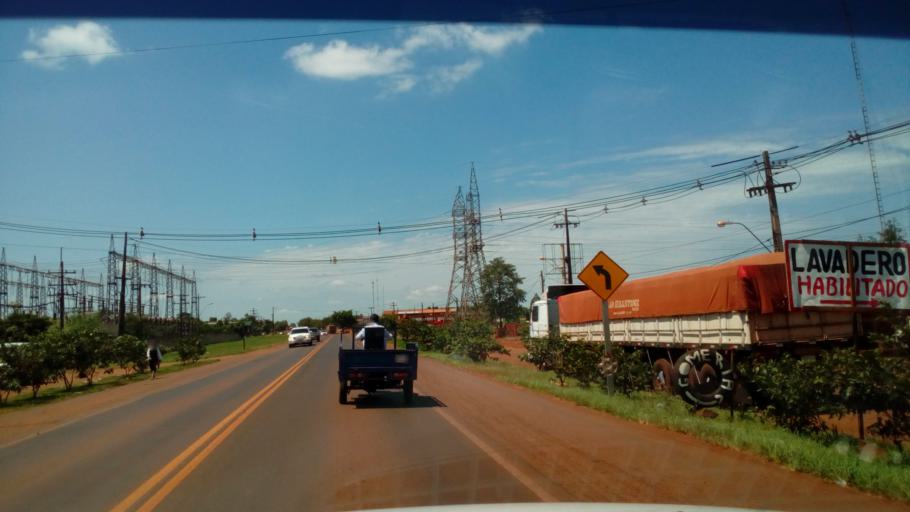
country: PY
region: Alto Parana
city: Colonia Yguazu
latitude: -25.4868
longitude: -54.8977
